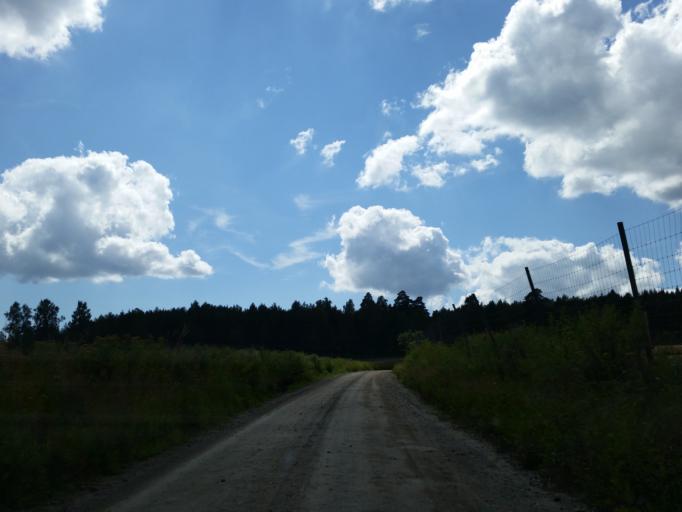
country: SE
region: Stockholm
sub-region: Sodertalje Kommun
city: Pershagen
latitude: 59.0641
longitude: 17.6612
